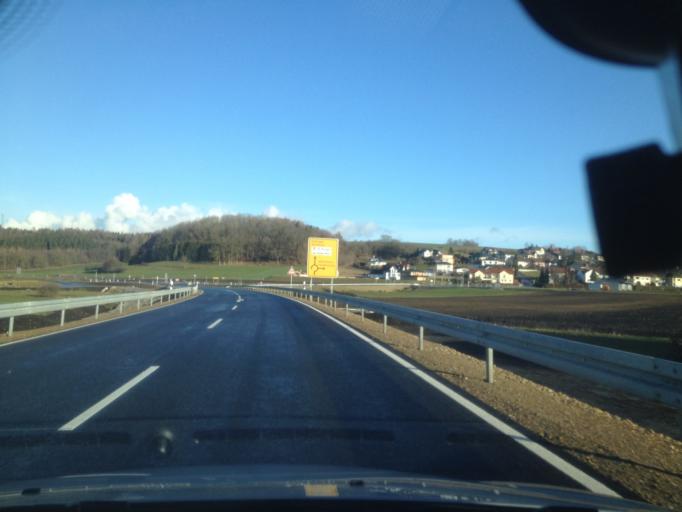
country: DE
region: Bavaria
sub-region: Swabia
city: Rofingen
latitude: 48.4321
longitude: 10.4362
